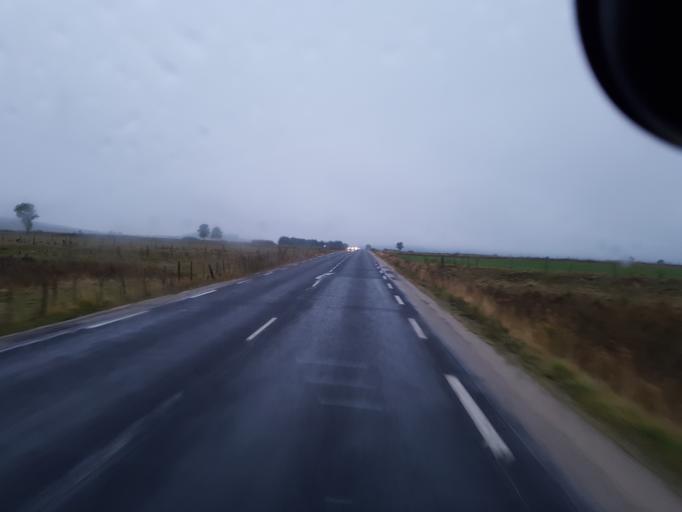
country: FR
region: Languedoc-Roussillon
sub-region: Departement de la Lozere
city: Langogne
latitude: 44.8146
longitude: 3.8760
